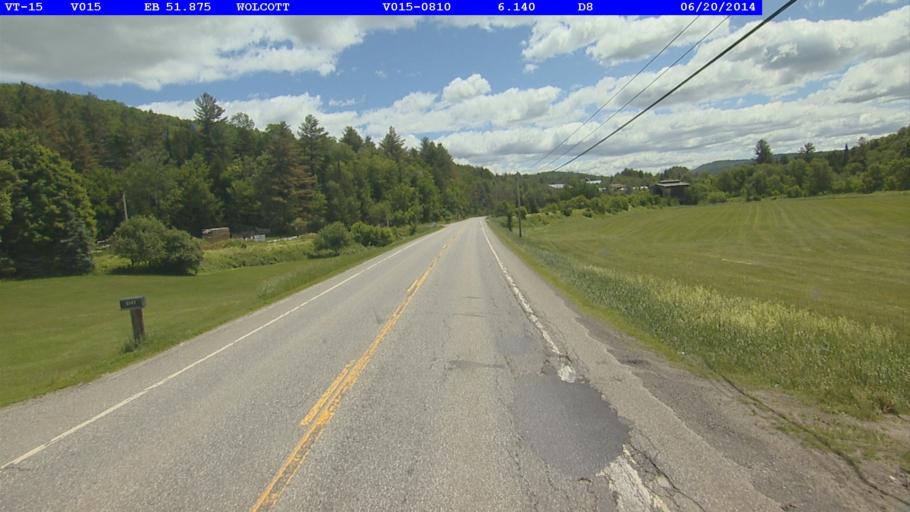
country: US
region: Vermont
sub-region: Caledonia County
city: Hardwick
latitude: 44.5340
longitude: -72.4305
